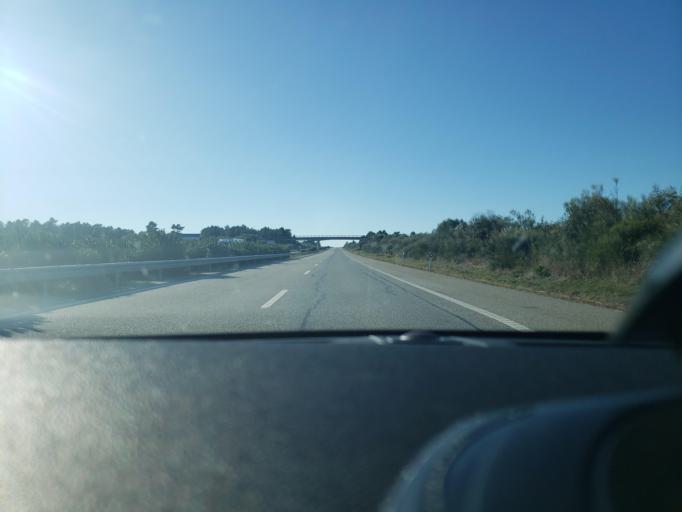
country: PT
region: Evora
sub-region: Borba
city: Borba
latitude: 38.8118
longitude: -7.5057
